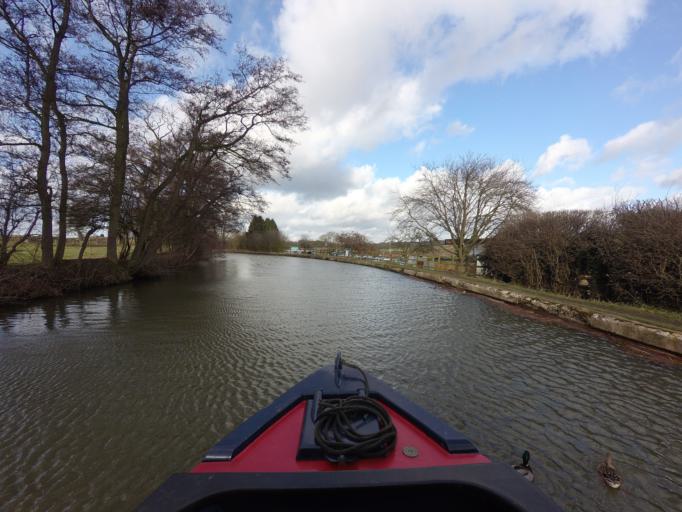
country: GB
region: England
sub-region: Northamptonshire
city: Long Buckby
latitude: 52.2357
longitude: -1.0789
